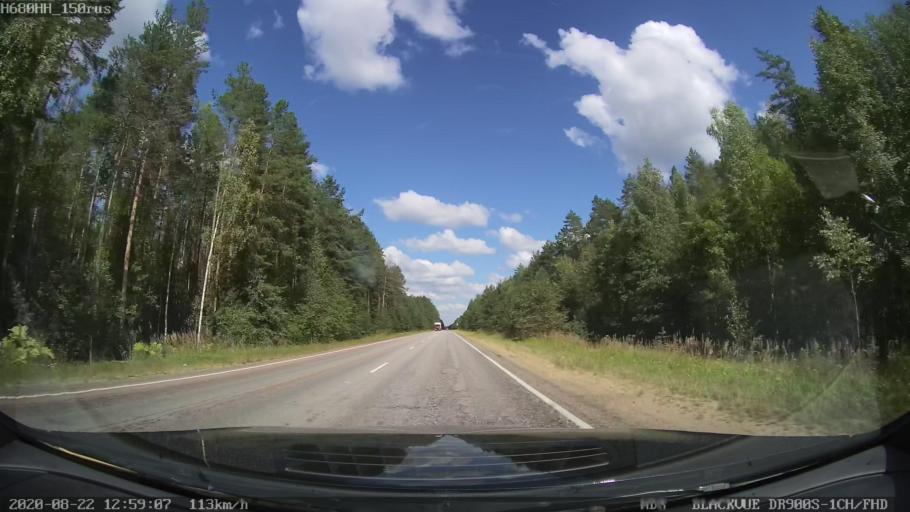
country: RU
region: Tverskaya
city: Bezhetsk
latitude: 57.6007
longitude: 36.3551
